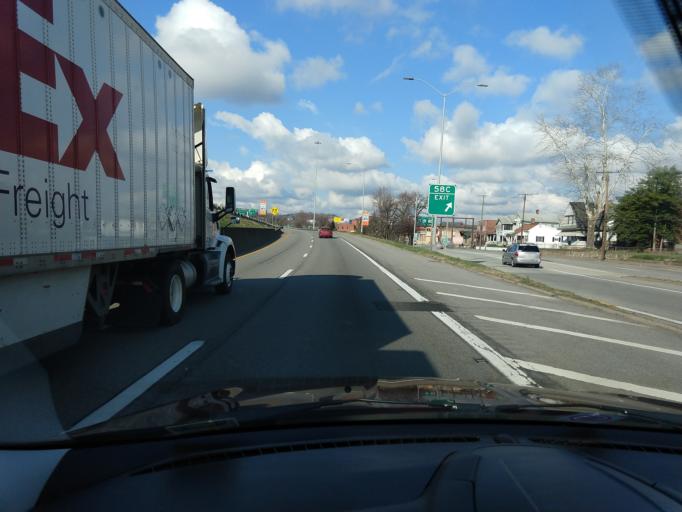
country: US
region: West Virginia
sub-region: Kanawha County
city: Charleston
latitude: 38.3596
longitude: -81.6365
